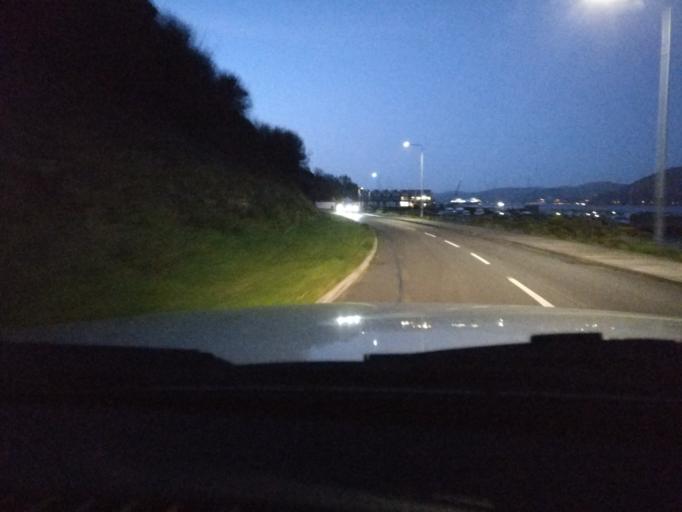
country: IE
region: Leinster
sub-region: Lu
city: Carlingford
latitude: 54.0492
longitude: -6.1910
